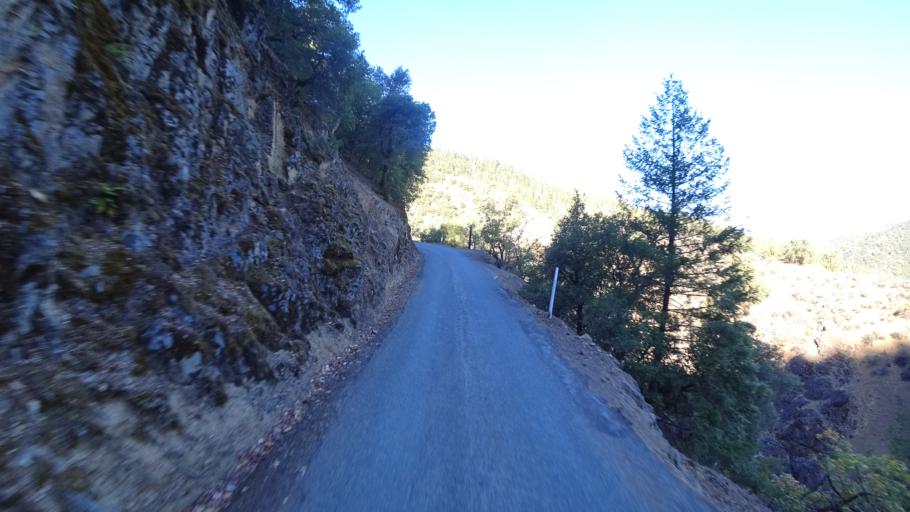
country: US
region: California
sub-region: Humboldt County
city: Willow Creek
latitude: 41.1851
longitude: -123.2157
